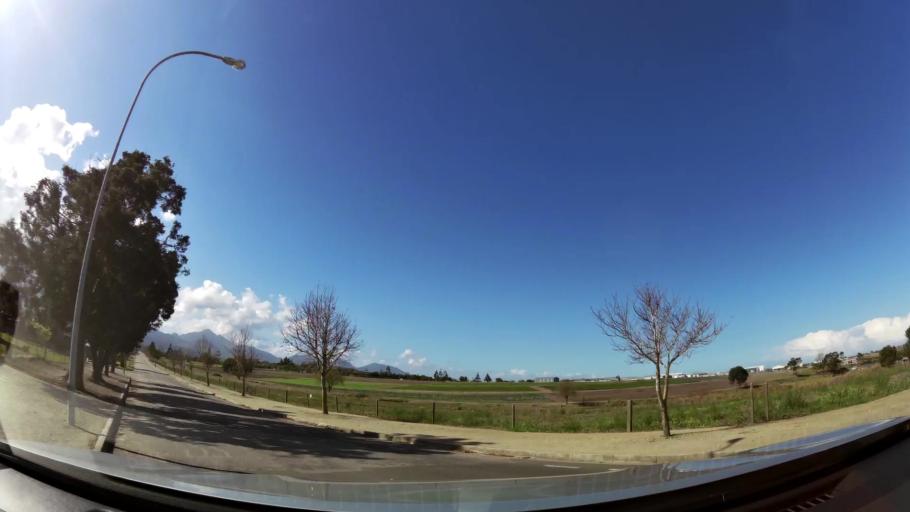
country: ZA
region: Western Cape
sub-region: Eden District Municipality
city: George
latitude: -33.9802
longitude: 22.4442
